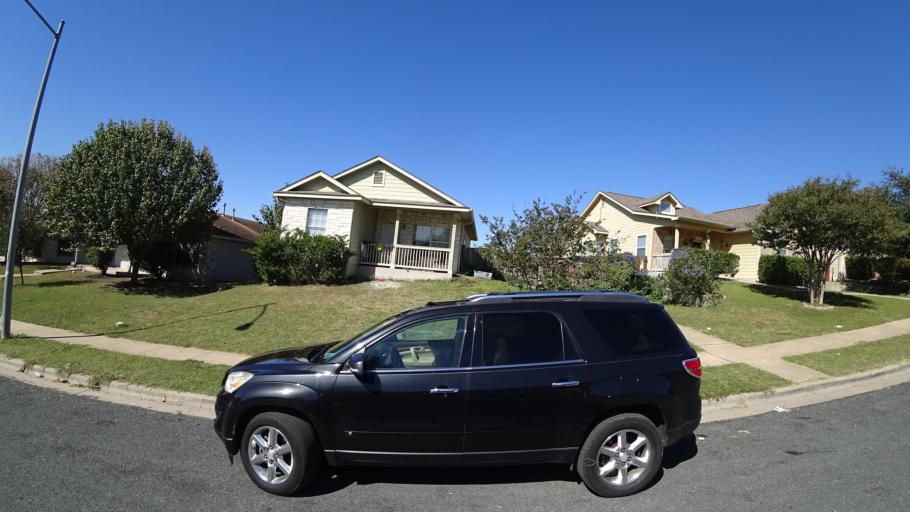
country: US
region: Texas
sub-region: Travis County
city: Hornsby Bend
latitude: 30.2891
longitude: -97.6473
